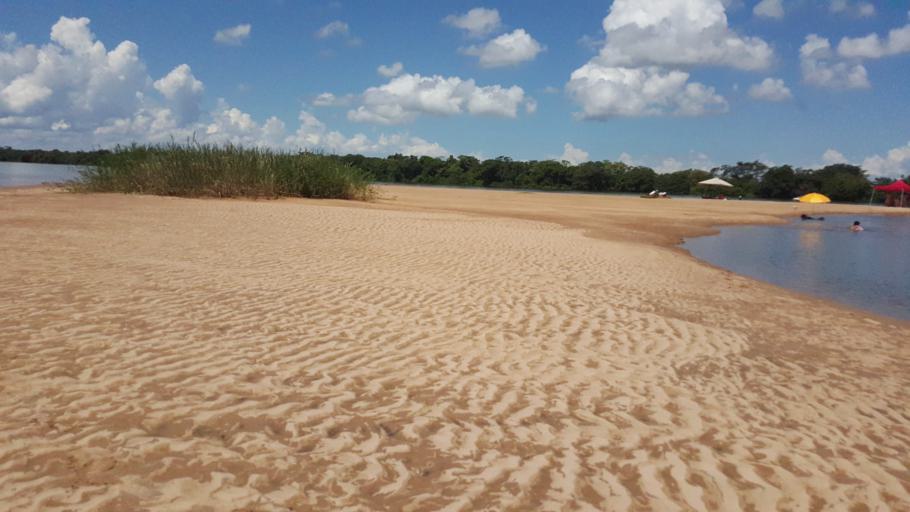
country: AR
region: Corrientes
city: Ituzaingo
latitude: -27.5751
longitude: -56.7067
